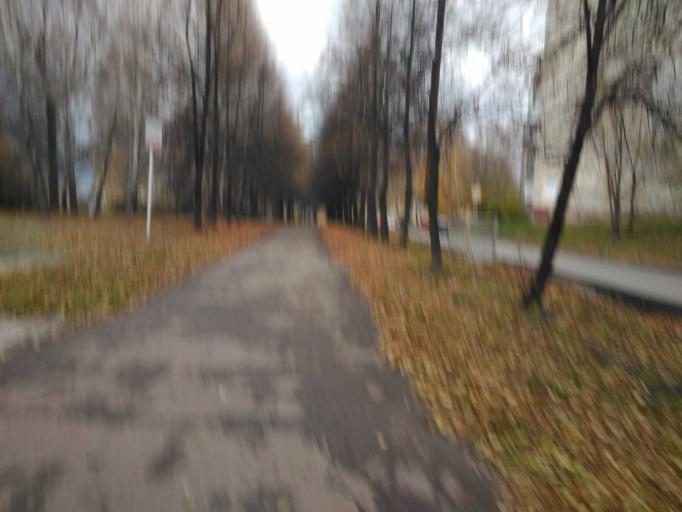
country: RU
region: Ulyanovsk
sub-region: Ulyanovskiy Rayon
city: Ulyanovsk
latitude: 54.3398
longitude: 48.3936
